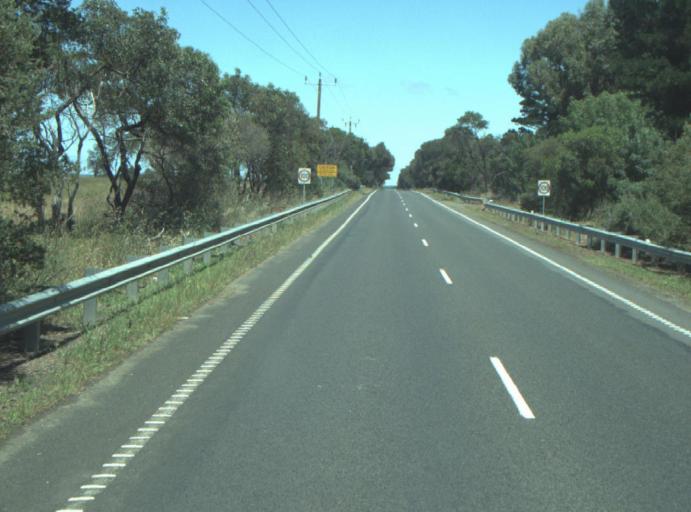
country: AU
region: Victoria
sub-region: Queenscliffe
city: Queenscliff
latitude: -38.1809
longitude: 144.6934
